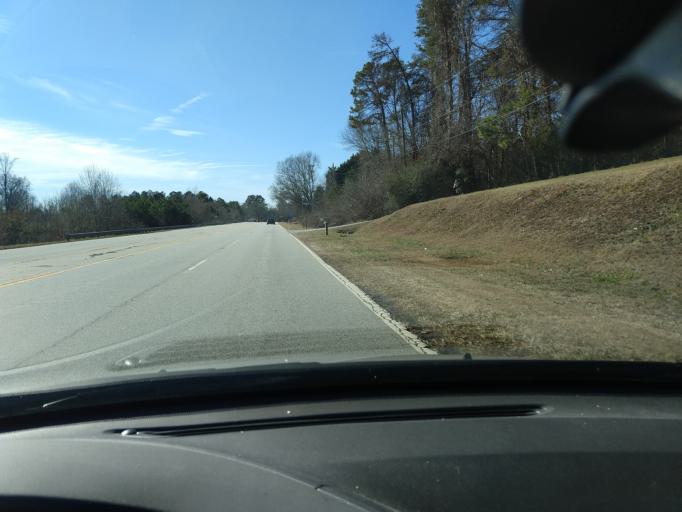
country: US
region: South Carolina
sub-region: Oconee County
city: Westminster
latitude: 34.6652
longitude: -83.0717
